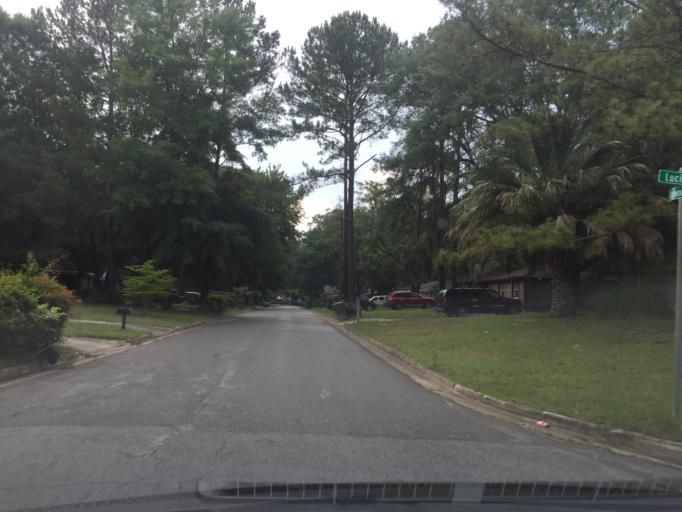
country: US
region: Georgia
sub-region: Chatham County
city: Montgomery
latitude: 31.9895
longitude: -81.1216
